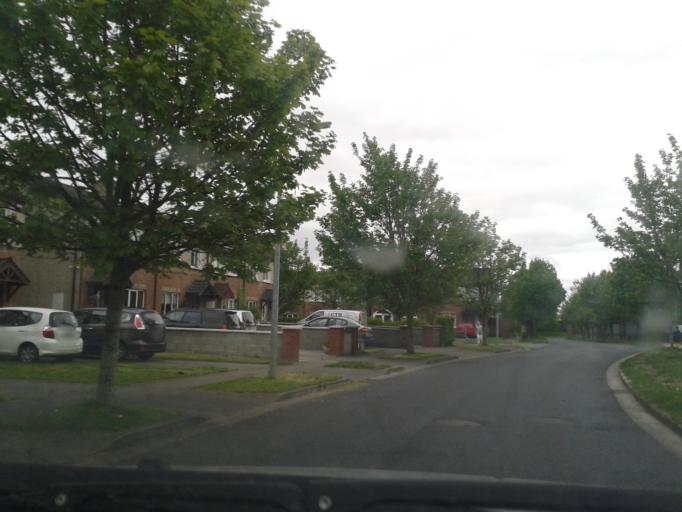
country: IE
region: Leinster
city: Clondalkin
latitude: 53.3213
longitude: -6.4250
